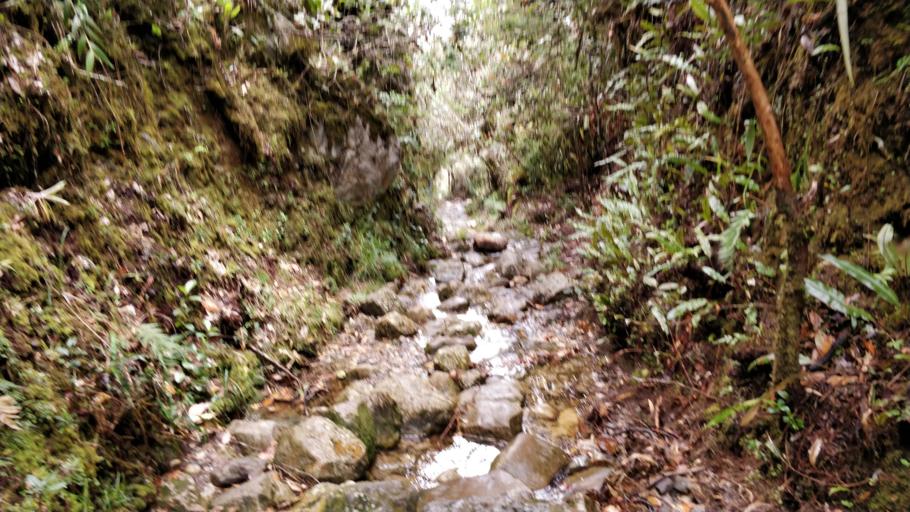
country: CO
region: Bogota D.C.
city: Bogota
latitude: 4.5356
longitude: -74.0514
